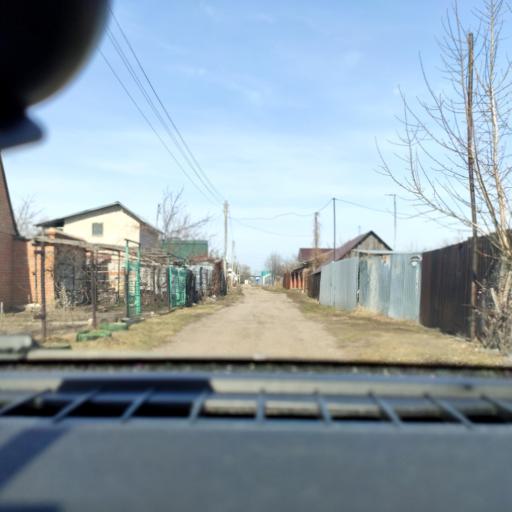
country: RU
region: Samara
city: Podstepki
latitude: 53.5175
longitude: 49.1078
